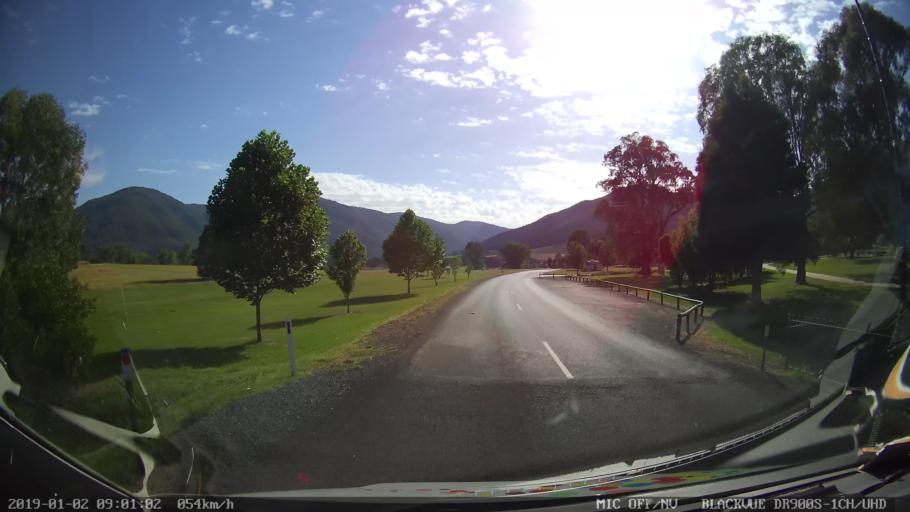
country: AU
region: New South Wales
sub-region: Tumut Shire
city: Tumut
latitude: -35.5781
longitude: 148.3019
